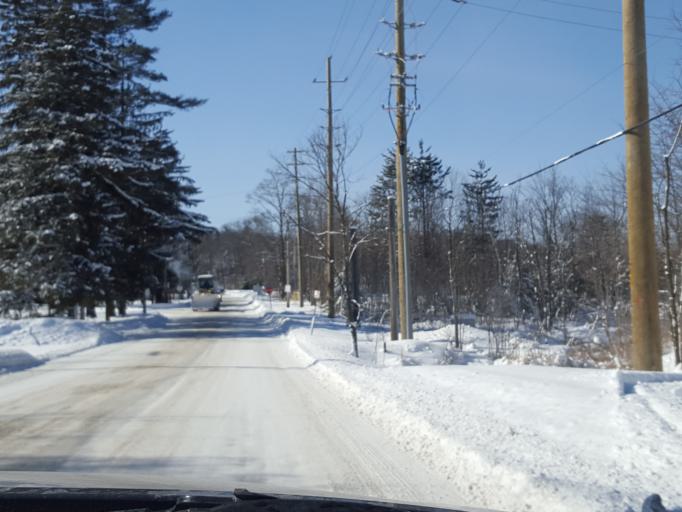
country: CA
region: Ontario
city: Gravenhurst
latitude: 44.9176
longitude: -79.3842
